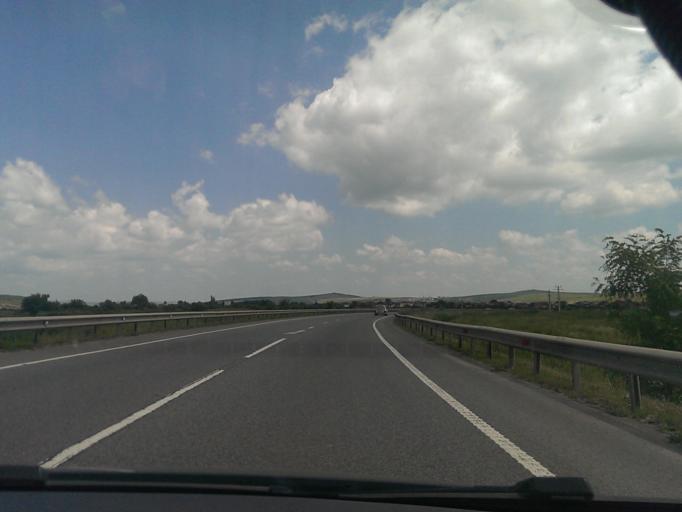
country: RO
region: Cluj
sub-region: Comuna Apahida
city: Sannicoara
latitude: 46.7850
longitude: 23.7081
